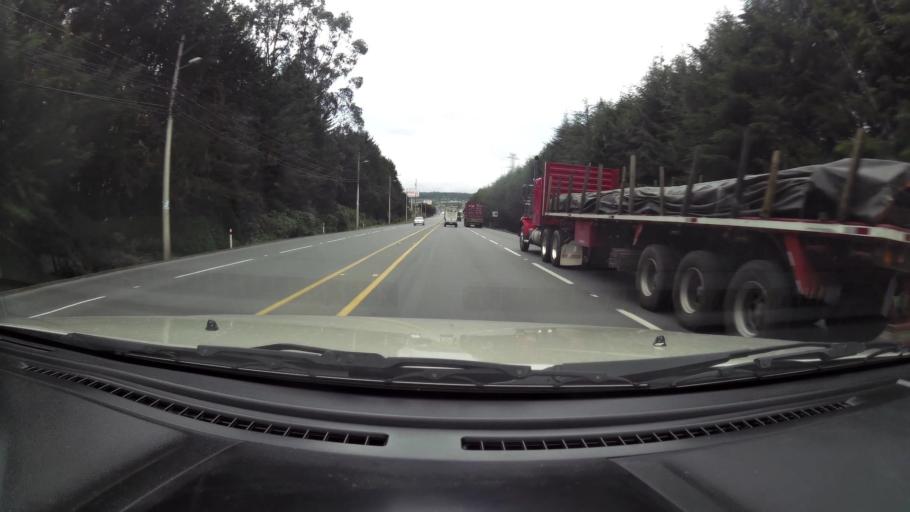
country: EC
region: Pichincha
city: Machachi
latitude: -0.4451
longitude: -78.6025
